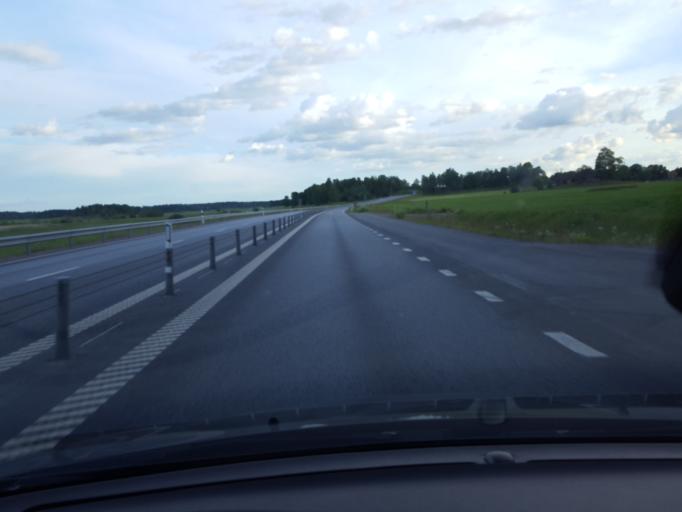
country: SE
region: Uppsala
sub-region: Osthammars Kommun
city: Gimo
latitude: 60.0439
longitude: 18.0442
